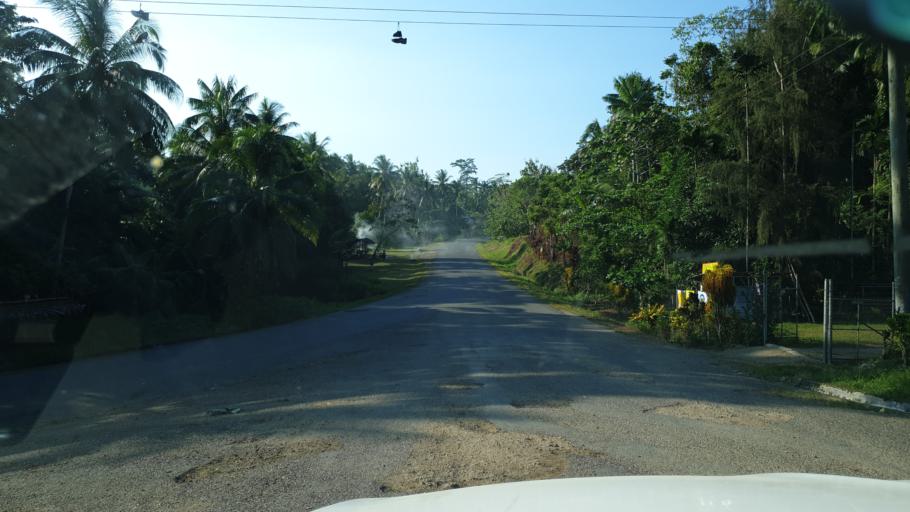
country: PG
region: East Sepik
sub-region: Wewak
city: Wewak
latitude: -3.7018
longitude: 143.6378
